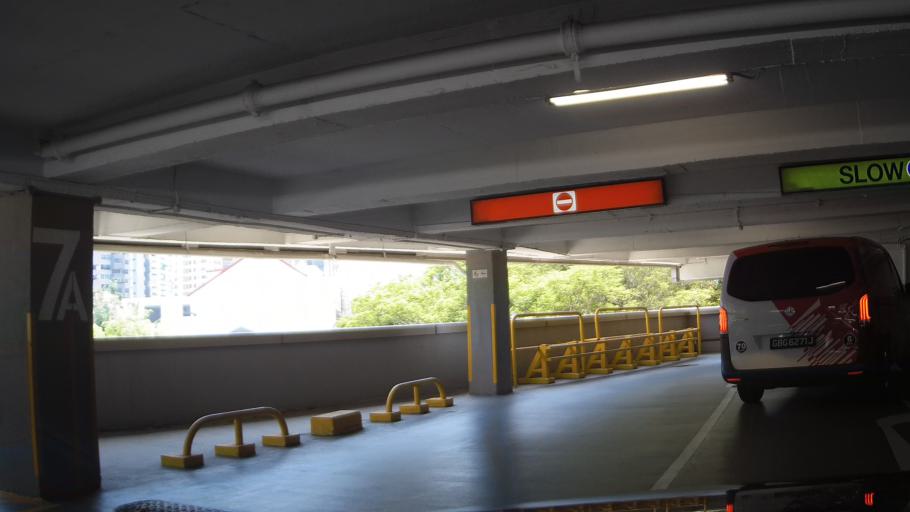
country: SG
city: Singapore
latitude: 1.2710
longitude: 103.8415
